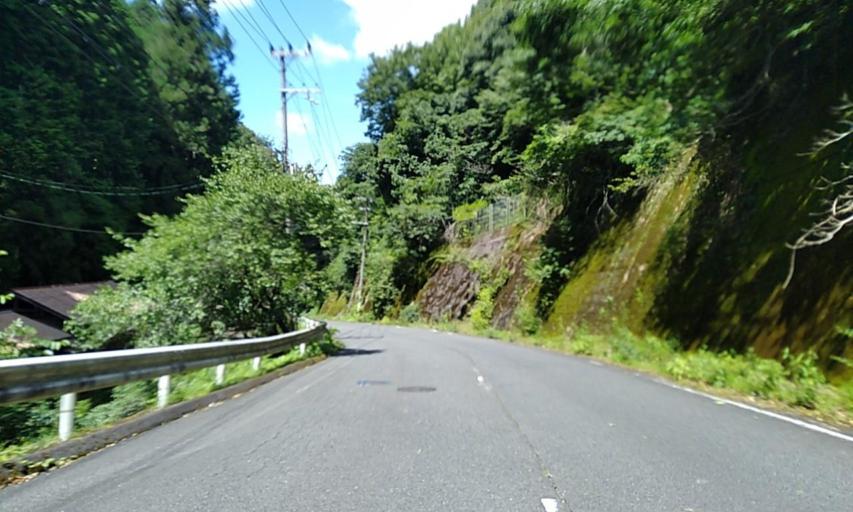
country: JP
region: Mie
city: Nabari
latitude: 34.7001
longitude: 136.0258
